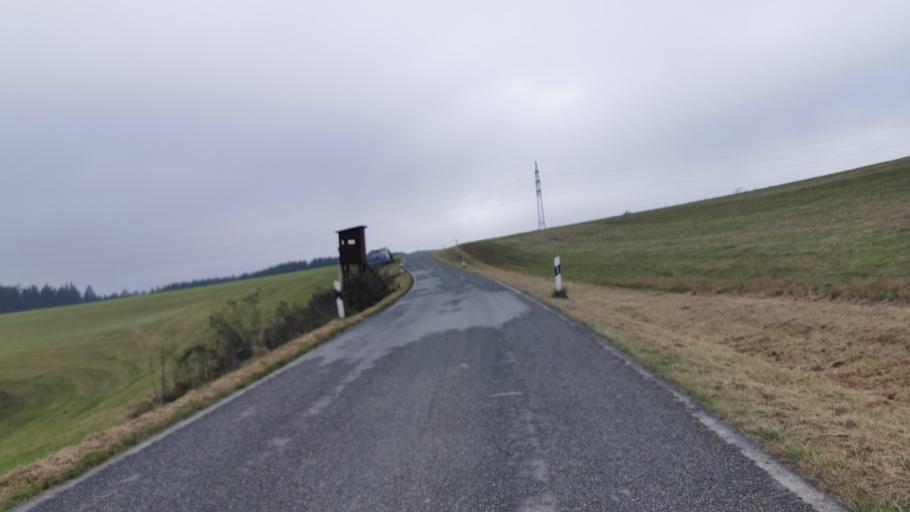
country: DE
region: Bavaria
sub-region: Upper Franconia
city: Ludwigsstadt
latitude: 50.4483
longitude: 11.3307
